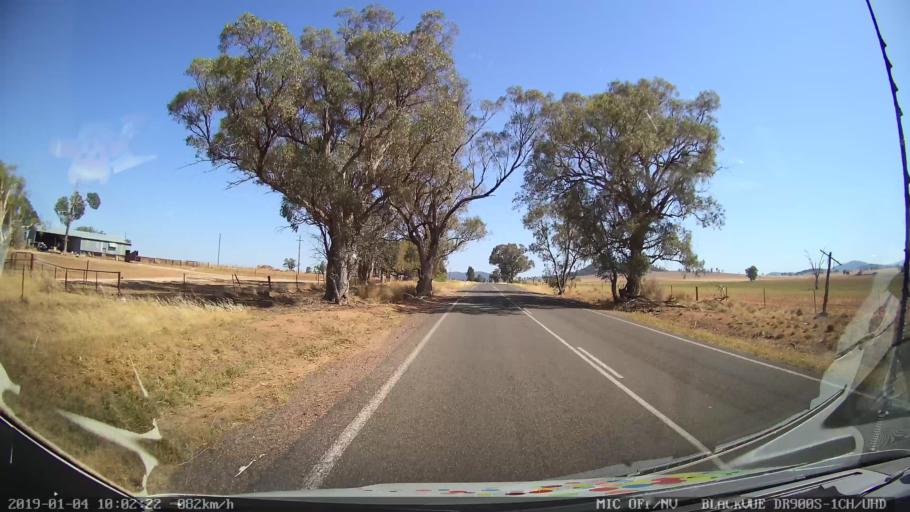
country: AU
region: New South Wales
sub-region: Cabonne
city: Canowindra
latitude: -33.4771
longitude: 148.3655
